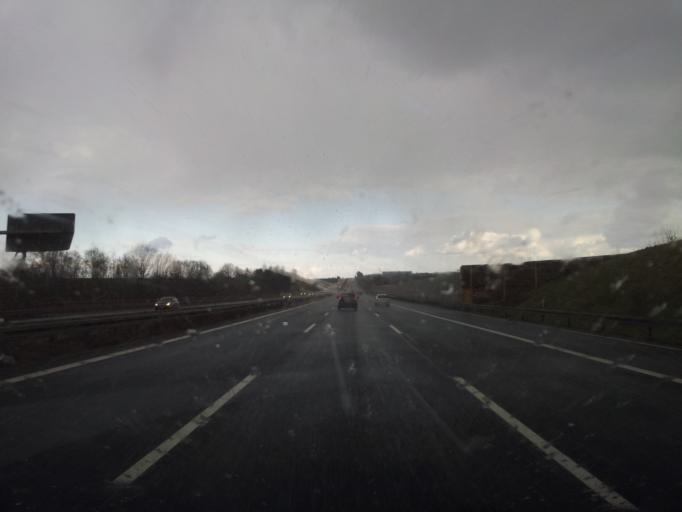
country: DE
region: Saxony
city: Wilsdruff
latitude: 51.0604
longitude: 13.5251
